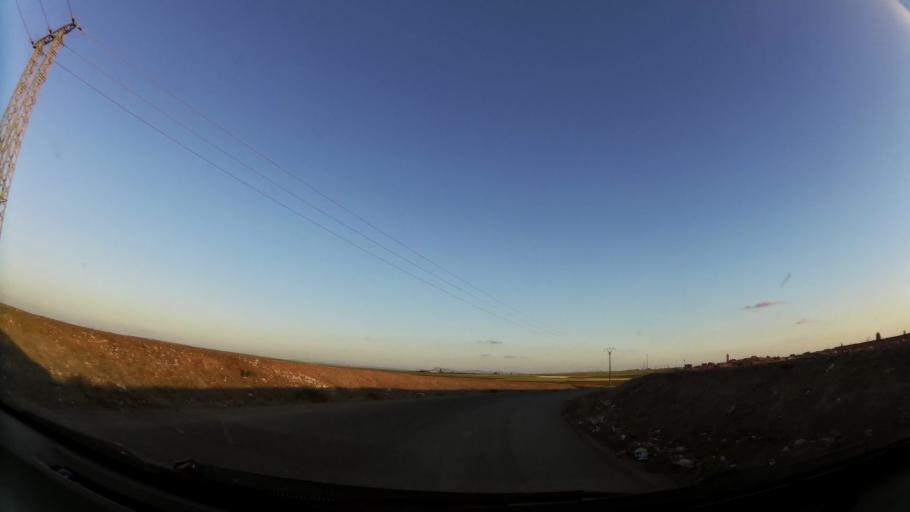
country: MA
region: Marrakech-Tensift-Al Haouz
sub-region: Kelaa-Des-Sraghna
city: Sidi Abdallah
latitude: 32.2382
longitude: -7.9283
